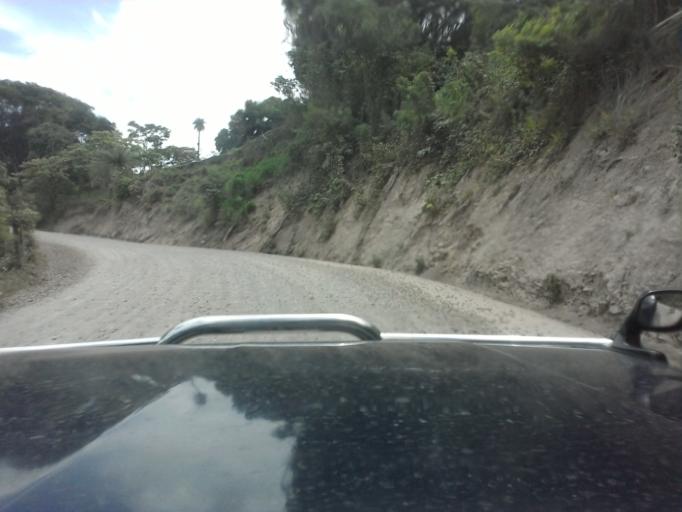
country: CR
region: Guanacaste
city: Juntas
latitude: 10.2189
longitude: -84.8535
